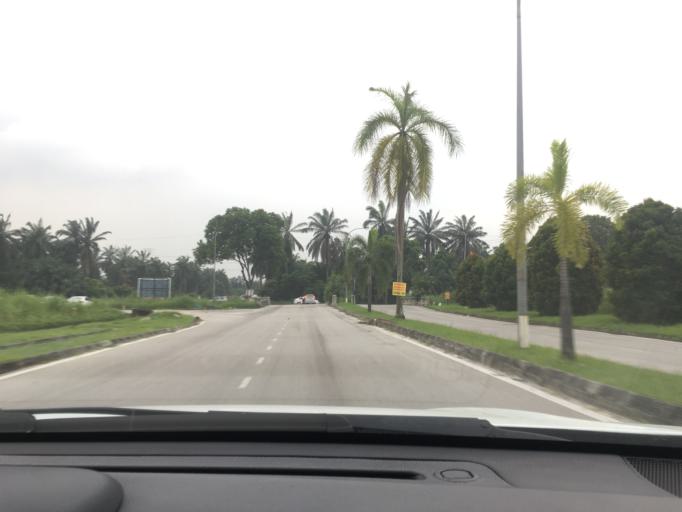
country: MY
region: Selangor
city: Klang
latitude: 3.1371
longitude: 101.4055
